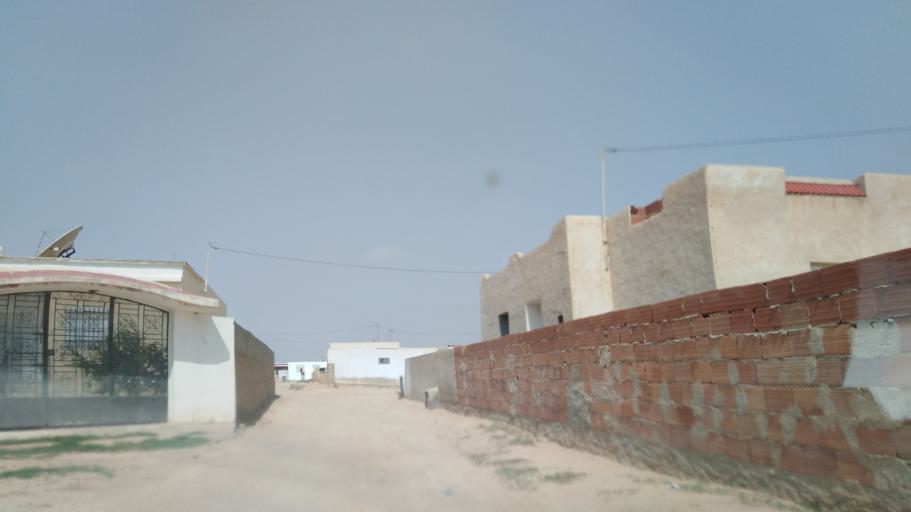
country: TN
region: Safaqis
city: Sfax
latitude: 34.6266
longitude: 10.5742
